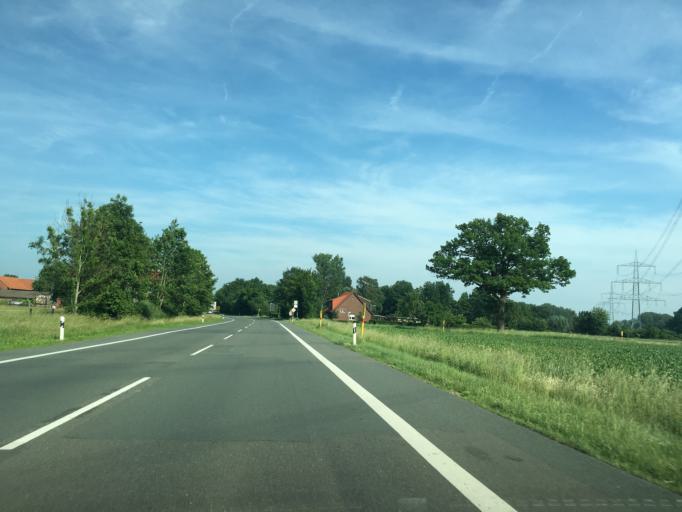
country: DE
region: North Rhine-Westphalia
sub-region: Regierungsbezirk Munster
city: Steinfurt
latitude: 52.1440
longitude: 7.4140
